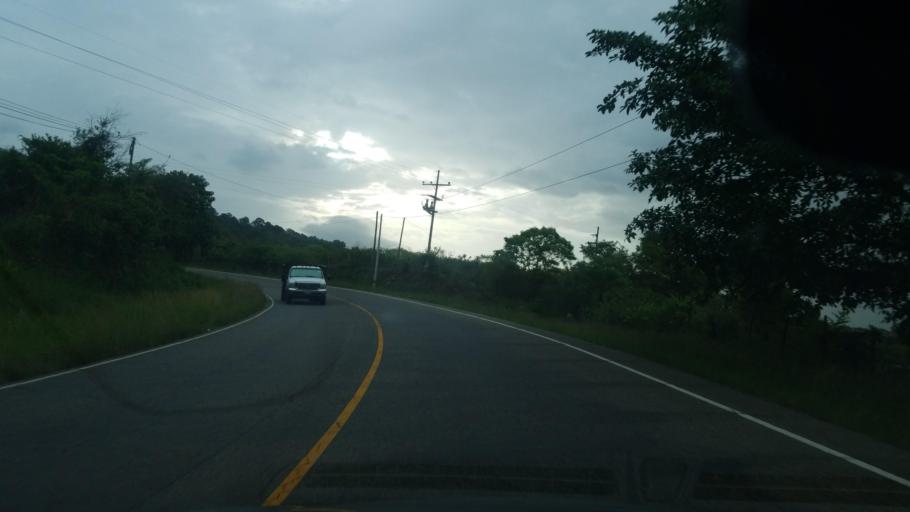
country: HN
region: Ocotepeque
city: Sinuapa
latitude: 14.4993
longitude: -89.2193
